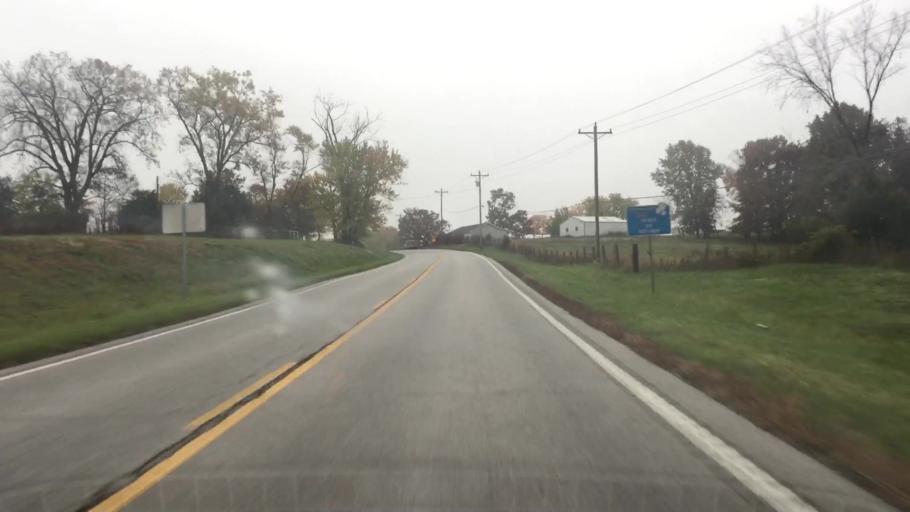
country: US
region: Missouri
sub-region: Callaway County
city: Fulton
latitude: 38.8592
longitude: -91.9984
